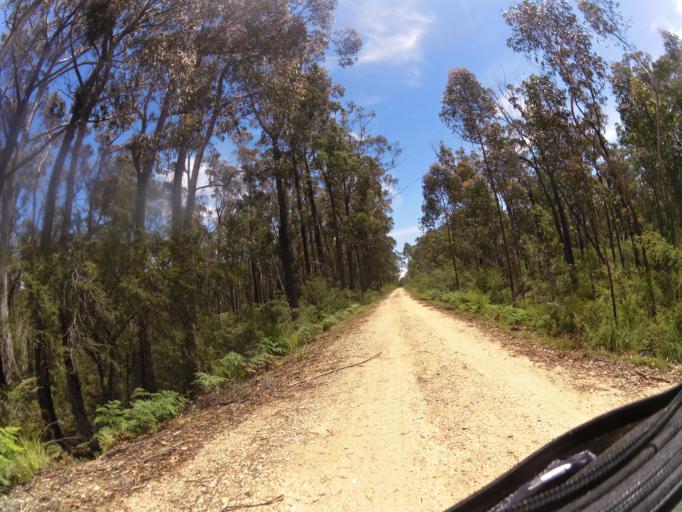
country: AU
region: Victoria
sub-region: East Gippsland
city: Lakes Entrance
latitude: -37.7591
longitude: 147.9523
